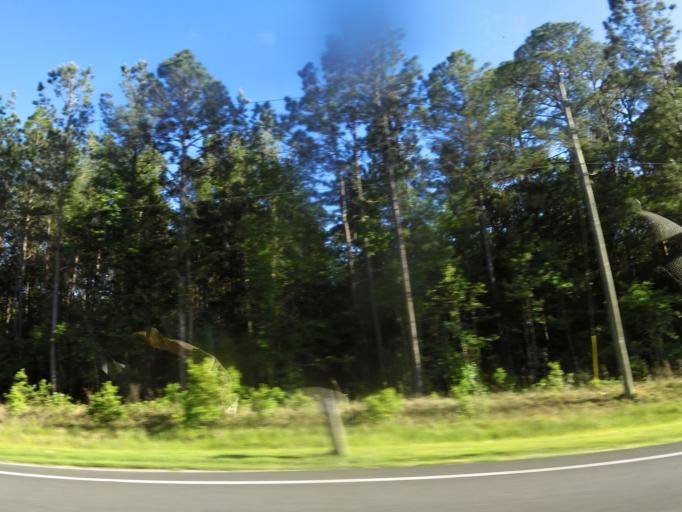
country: US
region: Florida
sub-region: Bradford County
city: Starke
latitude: 29.9274
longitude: -82.1034
